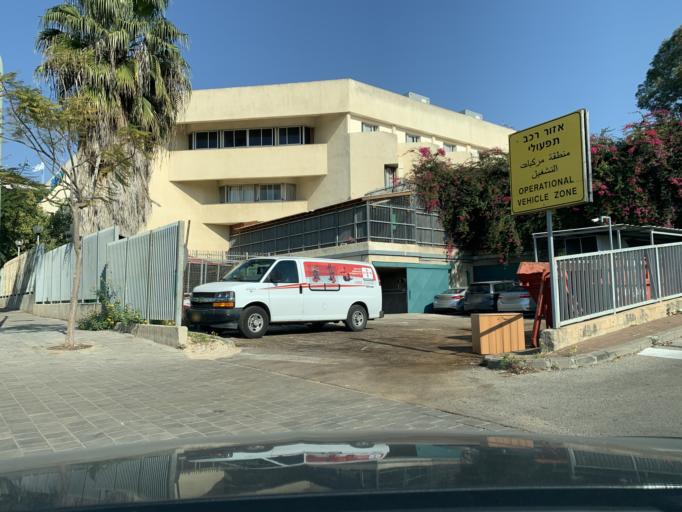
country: IL
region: Central District
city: Hod HaSharon
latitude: 32.1535
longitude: 34.8982
